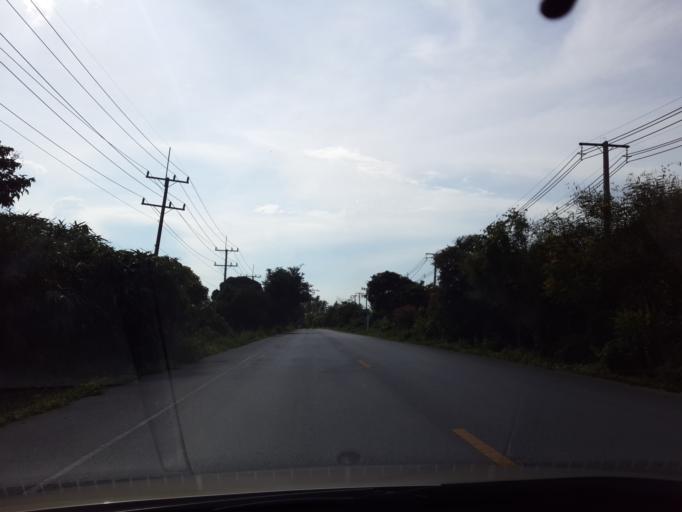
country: TH
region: Yala
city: Yala
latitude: 6.5015
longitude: 101.2749
